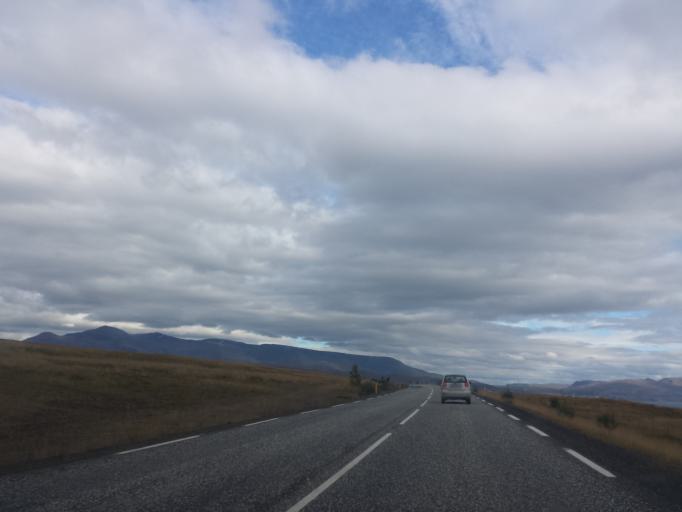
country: IS
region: Capital Region
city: Mosfellsbaer
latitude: 64.3408
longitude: -21.8225
